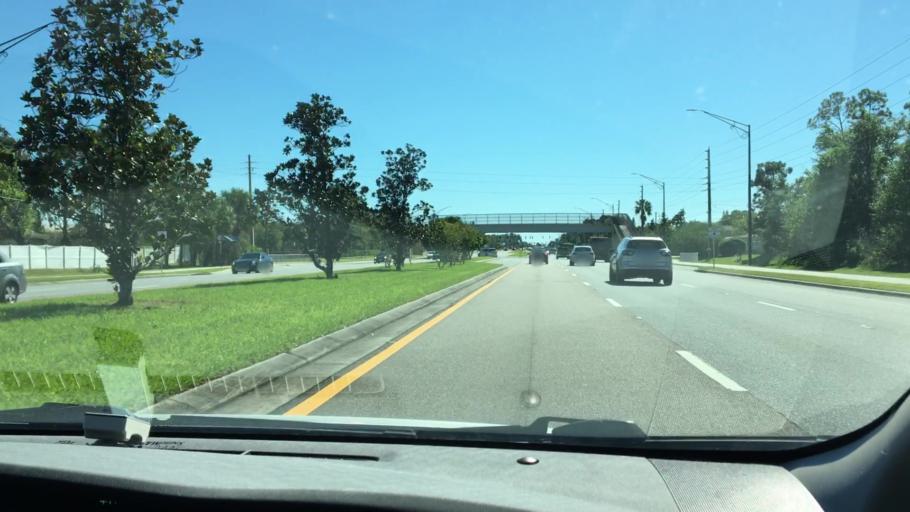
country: US
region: Florida
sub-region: Orange County
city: Conway
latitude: 28.4888
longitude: -81.3103
